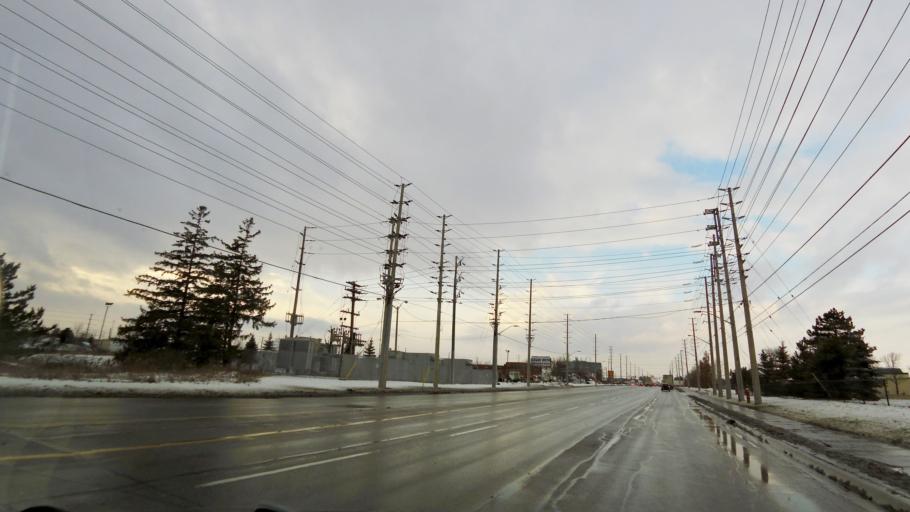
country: CA
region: Ontario
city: Brampton
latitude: 43.6634
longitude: -79.6817
